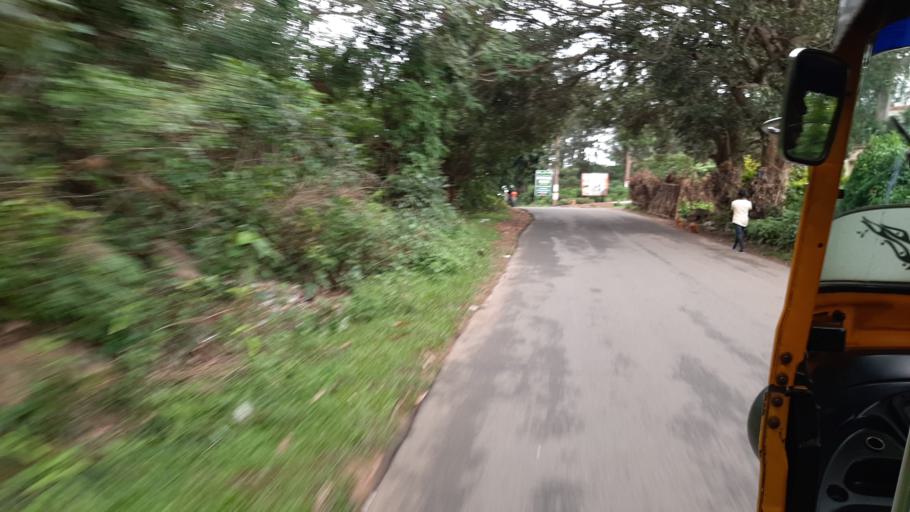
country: IN
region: Andhra Pradesh
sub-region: Vizianagaram District
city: Salur
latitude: 18.2389
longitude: 83.0134
